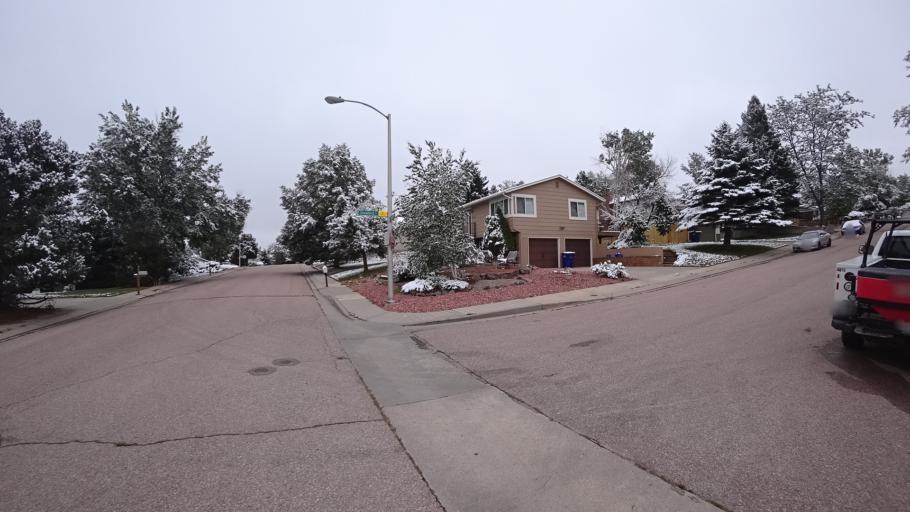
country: US
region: Colorado
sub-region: El Paso County
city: Colorado Springs
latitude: 38.9201
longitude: -104.7810
